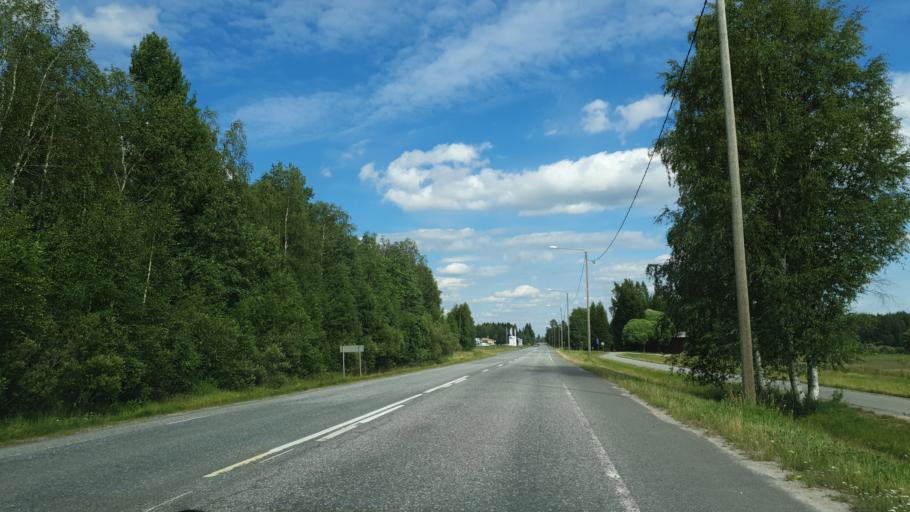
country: FI
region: Kainuu
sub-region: Kajaani
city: Kajaani
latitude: 64.2484
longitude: 27.7704
